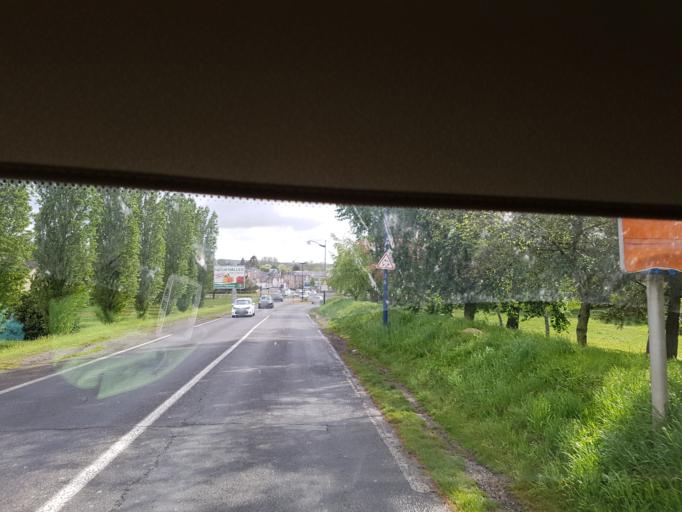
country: FR
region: Picardie
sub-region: Departement de l'Aisne
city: Soissons
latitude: 49.3706
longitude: 3.3207
